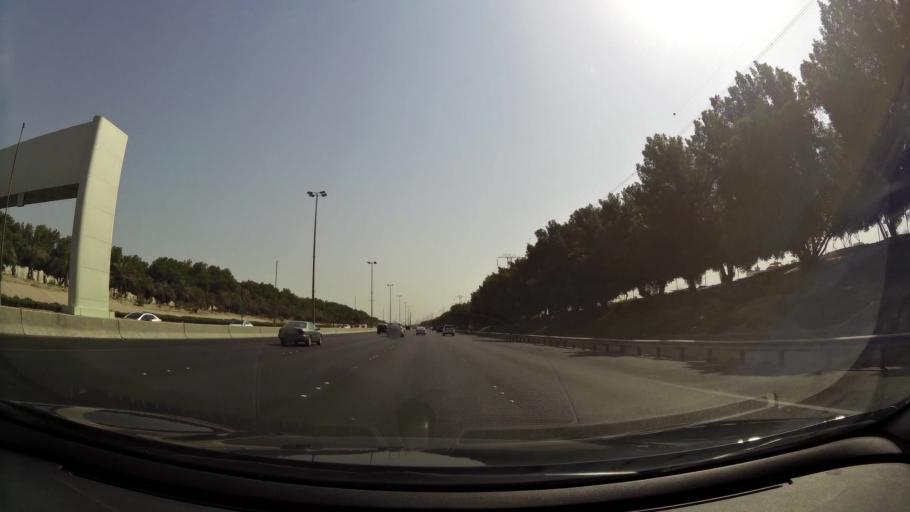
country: KW
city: Bayan
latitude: 29.2978
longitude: 48.0260
